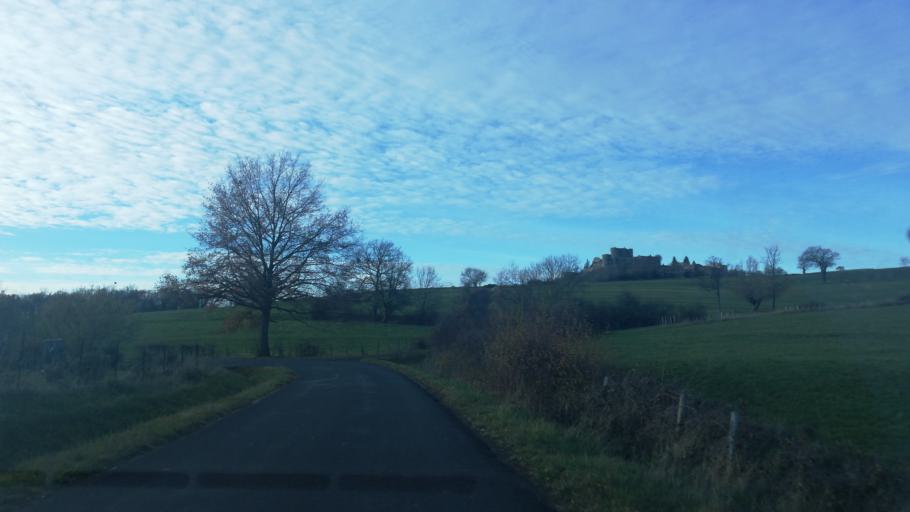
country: FR
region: Auvergne
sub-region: Departement du Puy-de-Dome
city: Billom
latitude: 45.6899
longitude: 3.3658
